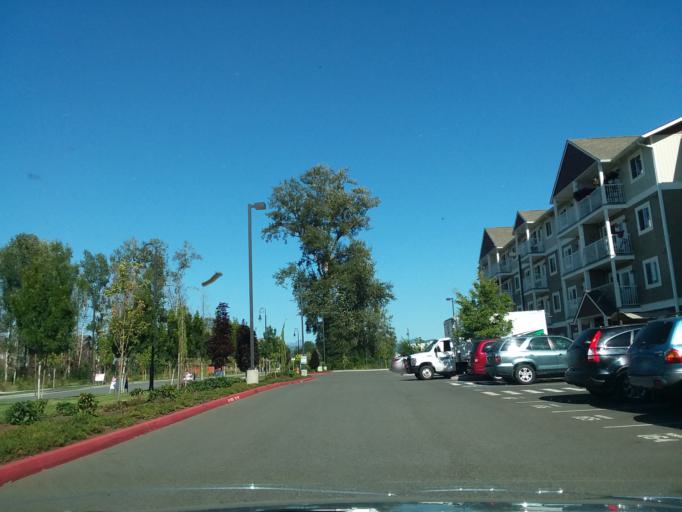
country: US
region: Washington
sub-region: Snohomish County
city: Smokey Point
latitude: 48.1536
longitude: -122.2013
